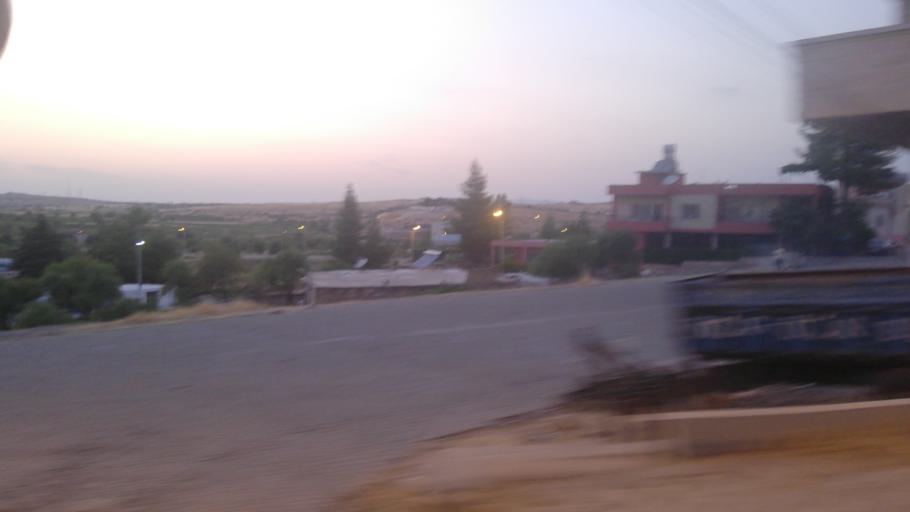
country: TR
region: Mardin
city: Kindirip
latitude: 37.4509
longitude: 41.2229
